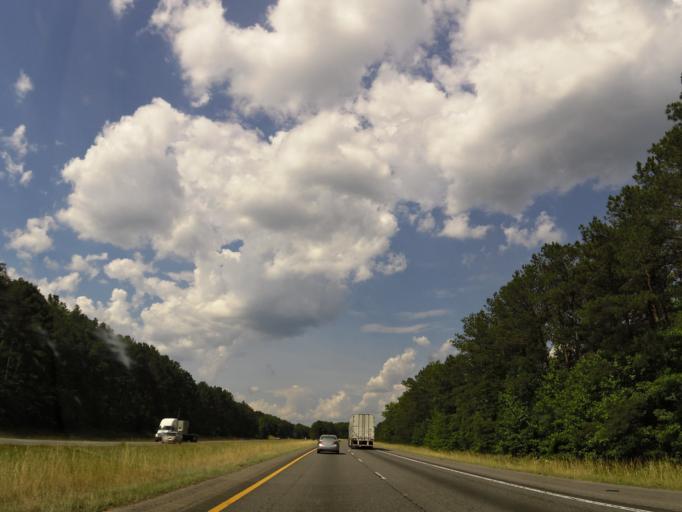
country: US
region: Alabama
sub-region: Hale County
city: Moundville
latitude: 33.0412
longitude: -87.7313
